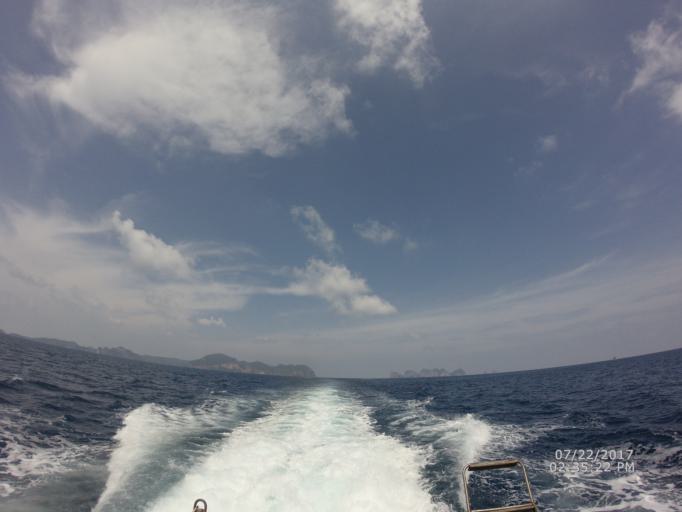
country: TH
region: Phangnga
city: Ban Phru Nai
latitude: 7.7440
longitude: 98.7038
